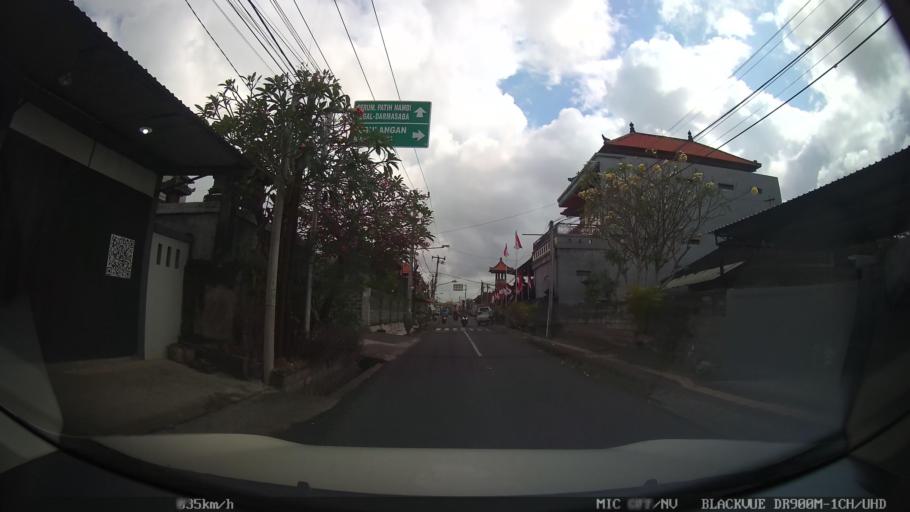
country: ID
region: Bali
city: Banjar Kertasari
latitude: -8.6211
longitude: 115.2025
